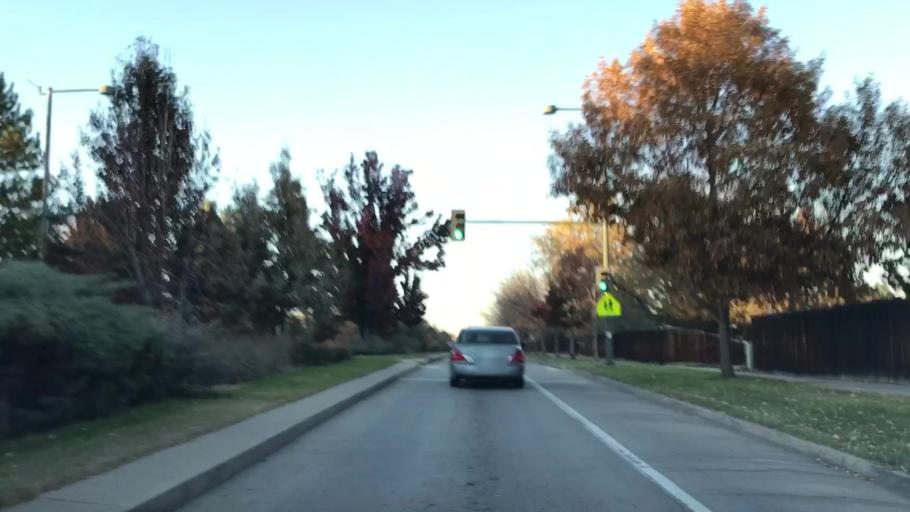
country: US
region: Colorado
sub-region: Arapahoe County
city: Glendale
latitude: 39.6581
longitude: -104.8846
